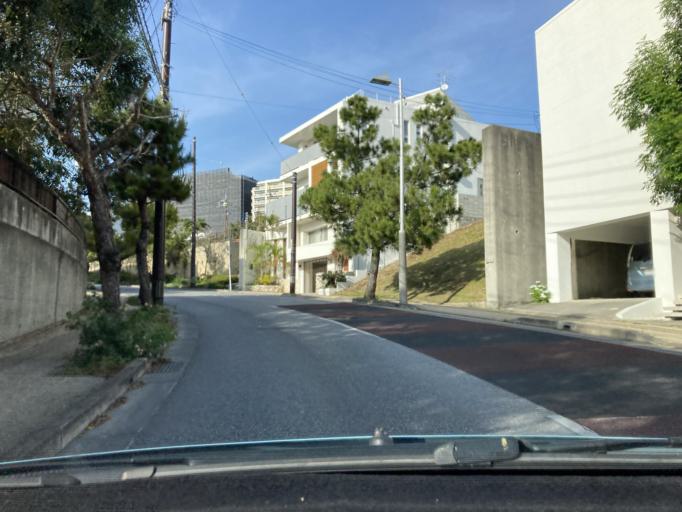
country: JP
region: Okinawa
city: Naha-shi
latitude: 26.2248
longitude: 127.6895
